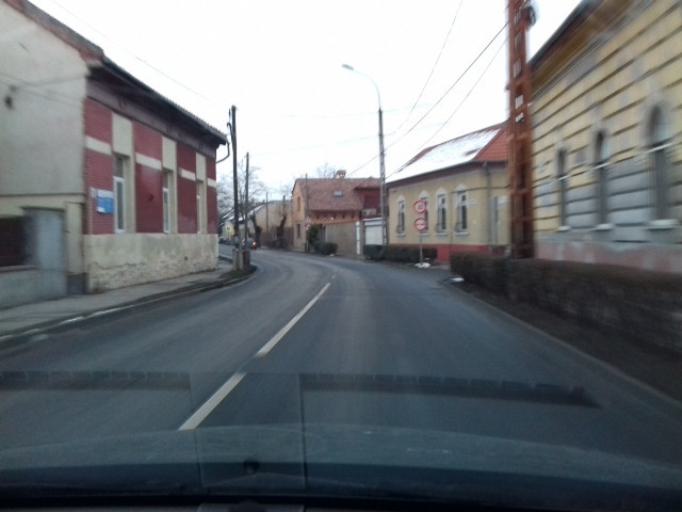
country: HU
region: Budapest
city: Budapest XV. keruelet
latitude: 47.5650
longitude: 19.1148
